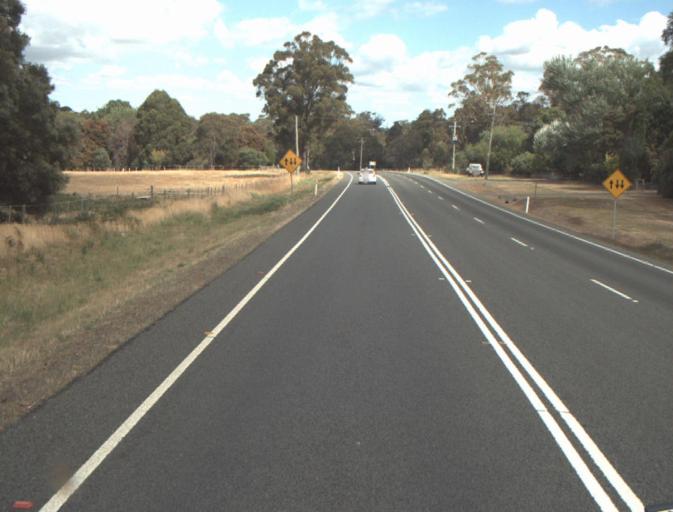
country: AU
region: Tasmania
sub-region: Launceston
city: Mayfield
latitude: -41.2847
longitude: 147.0400
